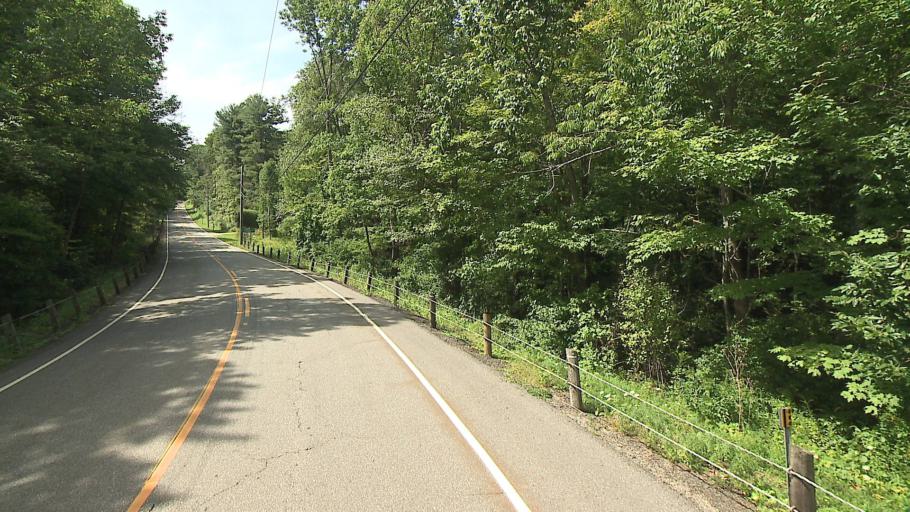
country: US
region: Connecticut
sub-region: Litchfield County
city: Litchfield
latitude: 41.7075
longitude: -73.1851
